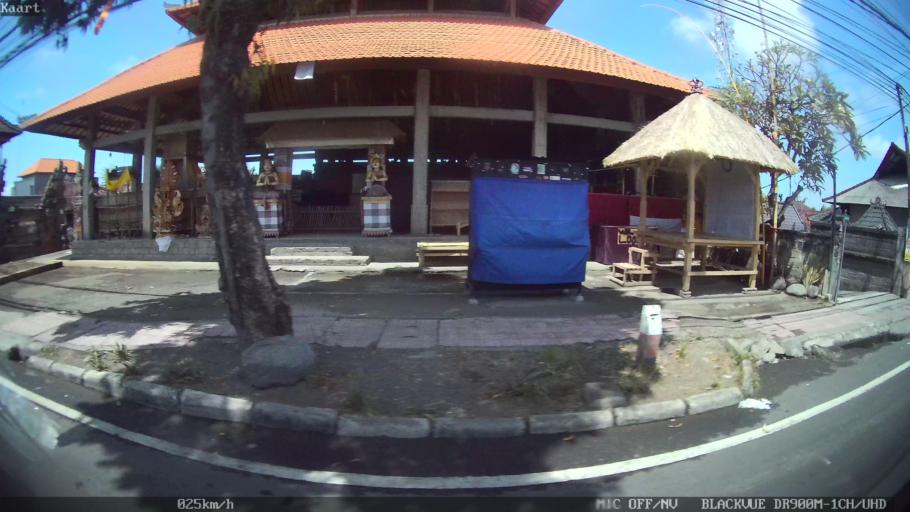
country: ID
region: Bali
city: Banjar Pasekan
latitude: -8.6034
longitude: 115.2766
